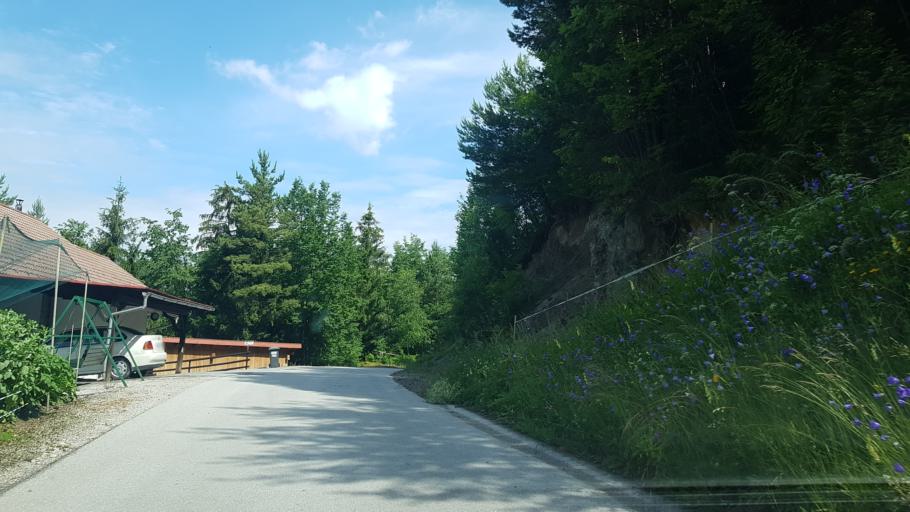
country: SI
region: Velenje
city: Velenje
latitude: 46.3836
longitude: 15.1739
